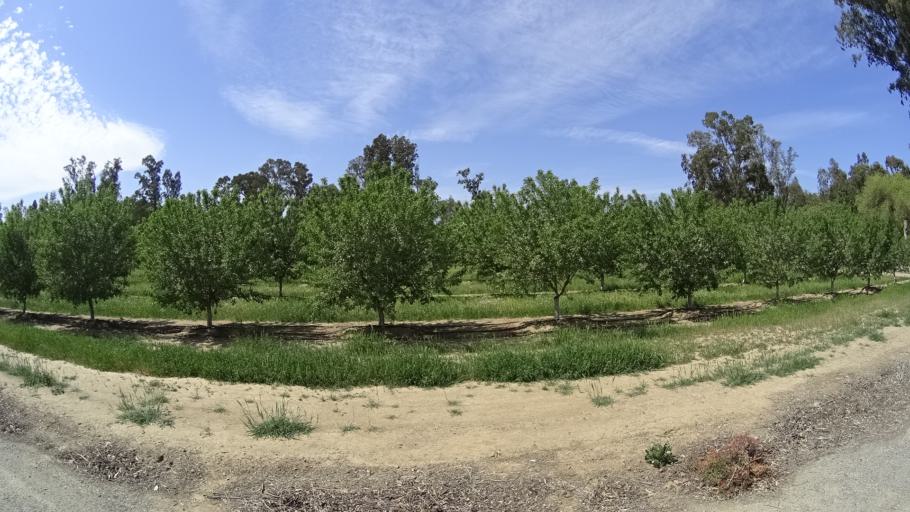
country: US
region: California
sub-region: Glenn County
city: Willows
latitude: 39.5840
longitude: -122.1970
